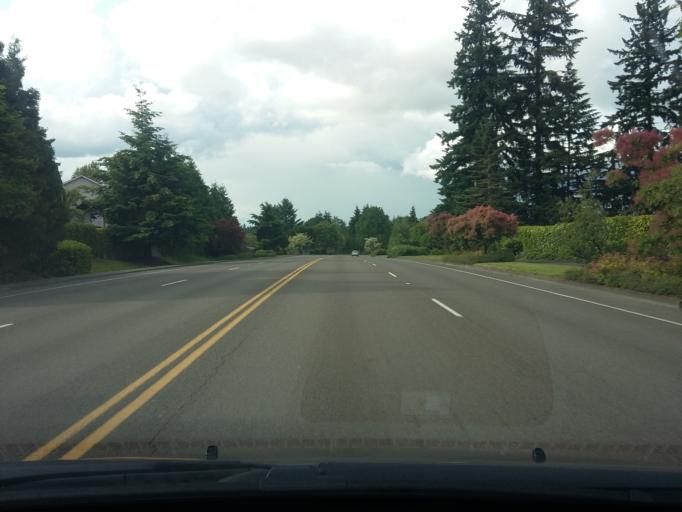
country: US
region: Washington
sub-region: Clark County
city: Walnut Grove
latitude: 45.6734
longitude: -122.6032
